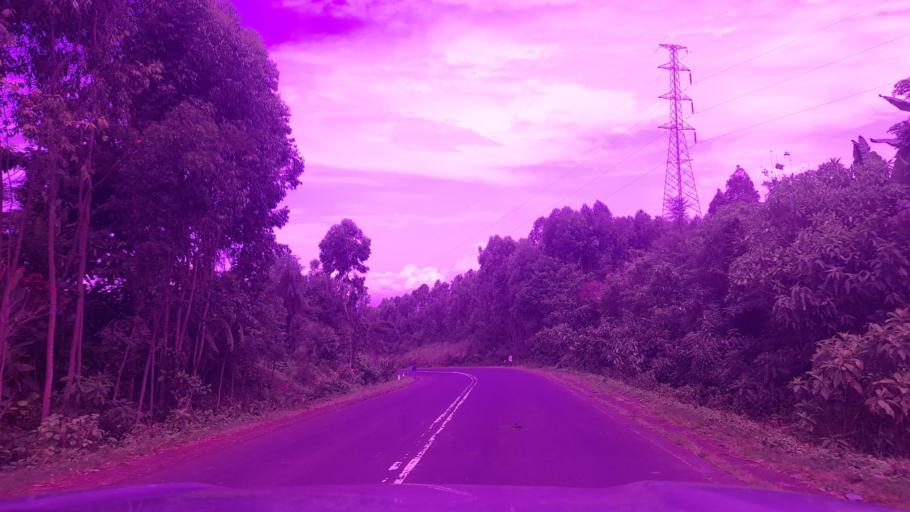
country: ET
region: Oromiya
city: Jima
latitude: 7.5210
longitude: 36.5345
